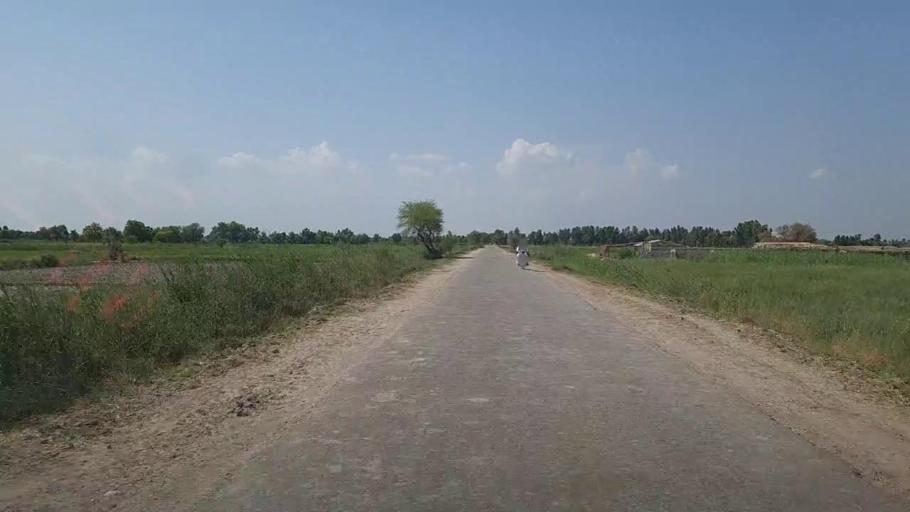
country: PK
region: Sindh
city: Khairpur
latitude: 28.0780
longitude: 69.6377
